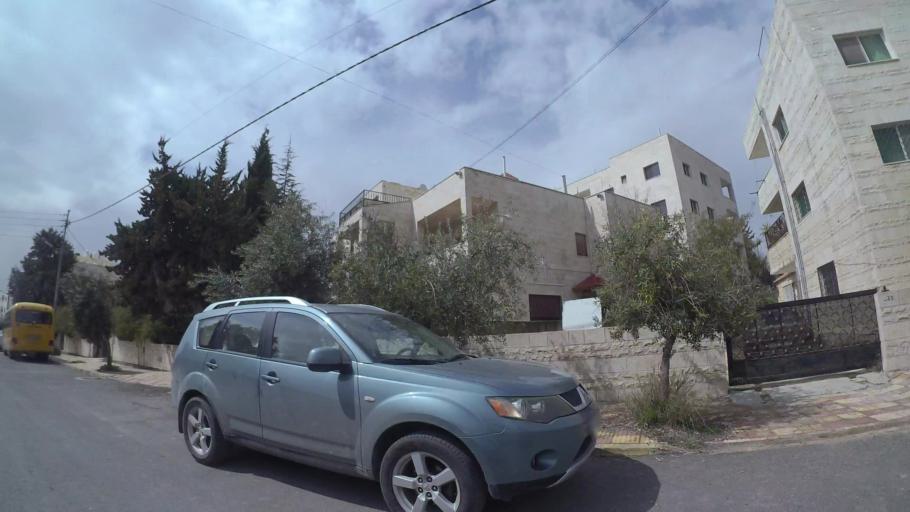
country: JO
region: Amman
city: Umm as Summaq
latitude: 31.8998
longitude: 35.8406
